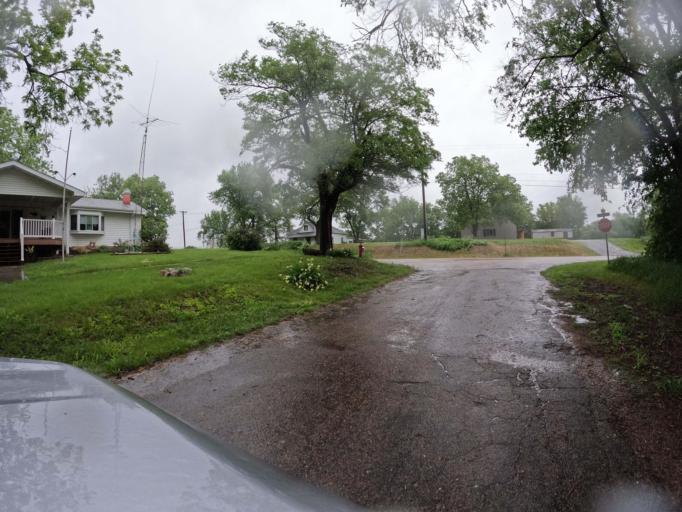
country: US
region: Nebraska
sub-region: Gage County
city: Wymore
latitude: 40.1242
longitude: -96.6541
